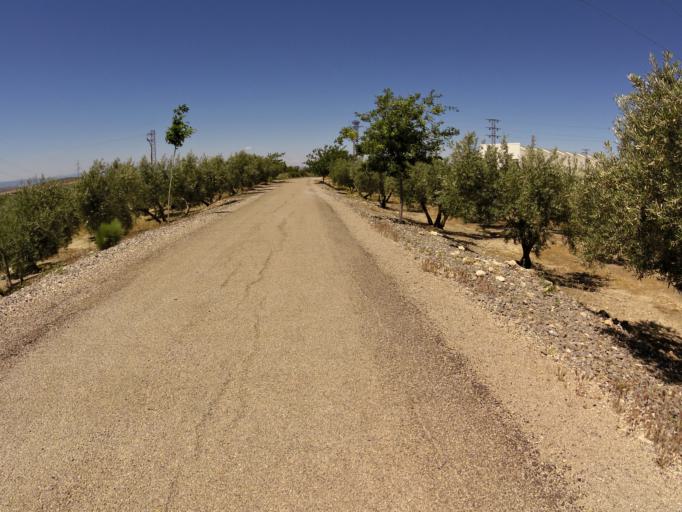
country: ES
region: Andalusia
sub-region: Provincia de Jaen
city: Torre del Campo
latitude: 37.7857
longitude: -3.8892
